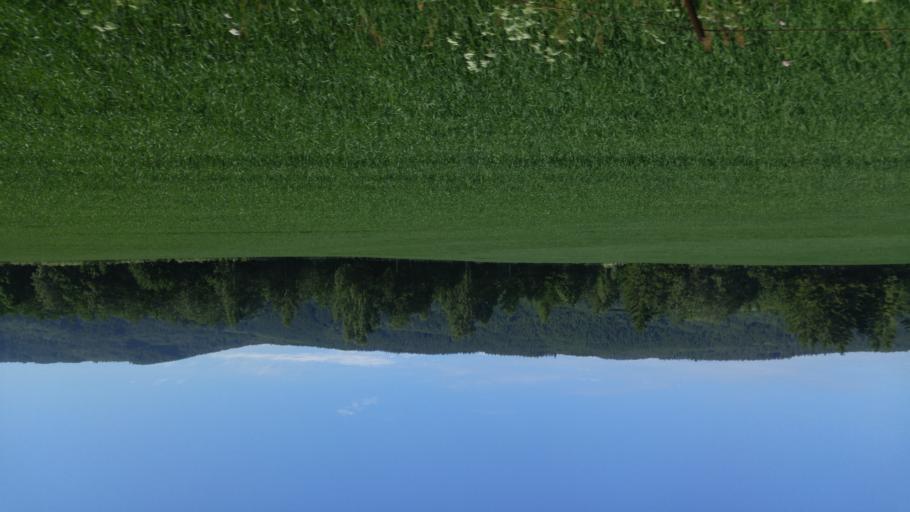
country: NO
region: Nord-Trondelag
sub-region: Stjordal
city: Stjordalshalsen
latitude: 63.4600
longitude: 11.1537
